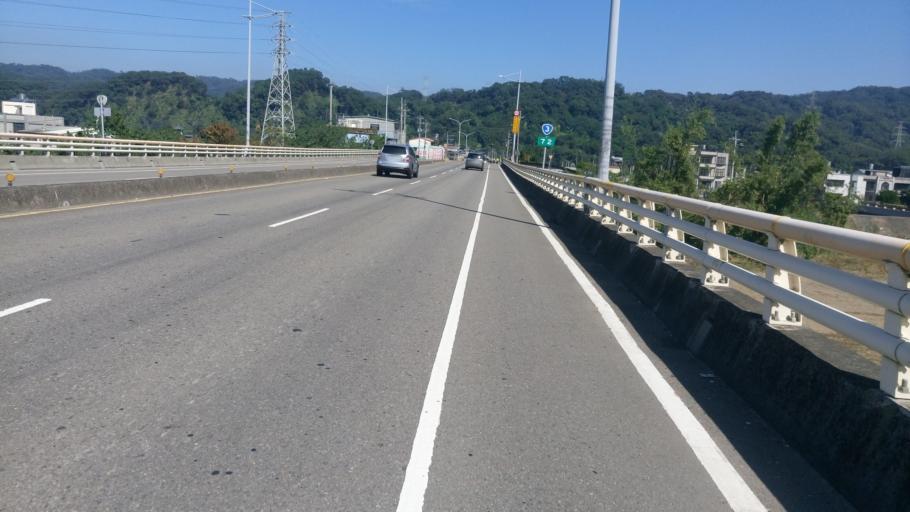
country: TW
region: Taiwan
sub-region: Hsinchu
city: Zhubei
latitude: 24.7232
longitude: 121.1244
